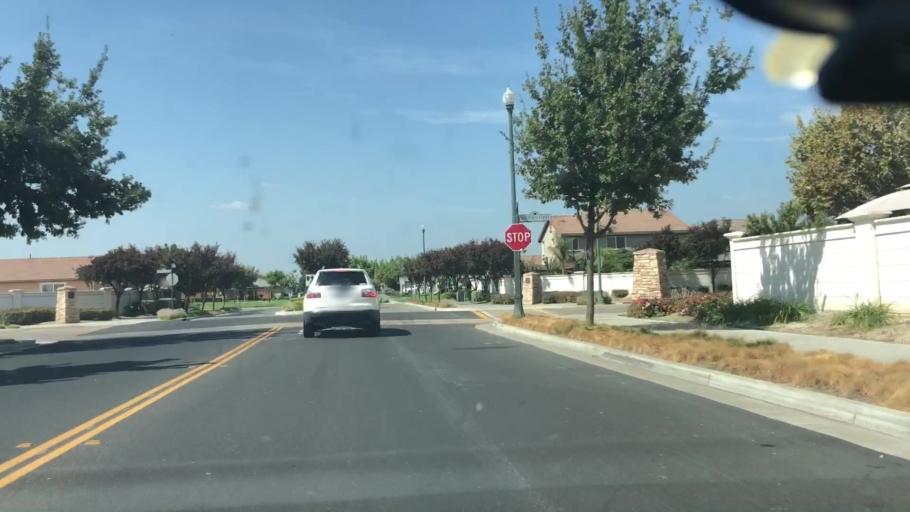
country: US
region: California
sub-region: San Joaquin County
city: Lathrop
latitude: 37.8144
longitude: -121.3073
